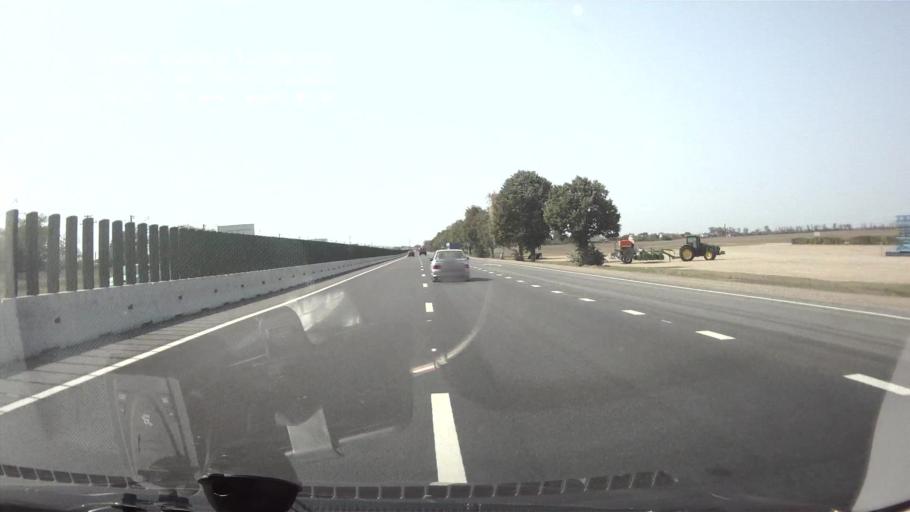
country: RU
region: Adygeya
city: Khatukay
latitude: 45.2202
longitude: 39.6001
